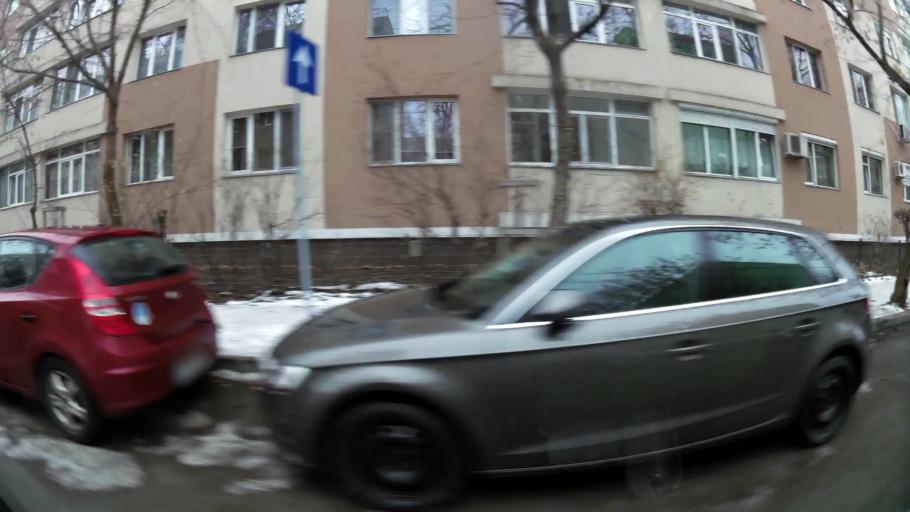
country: RO
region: Ilfov
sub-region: Comuna Chiajna
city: Rosu
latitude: 44.4440
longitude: 26.0309
